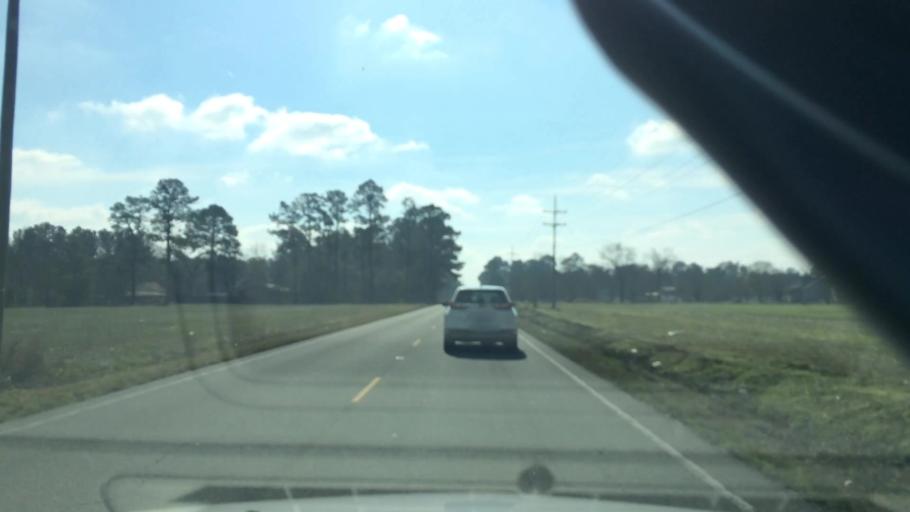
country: US
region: North Carolina
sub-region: Duplin County
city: Beulaville
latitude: 34.9028
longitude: -77.7796
